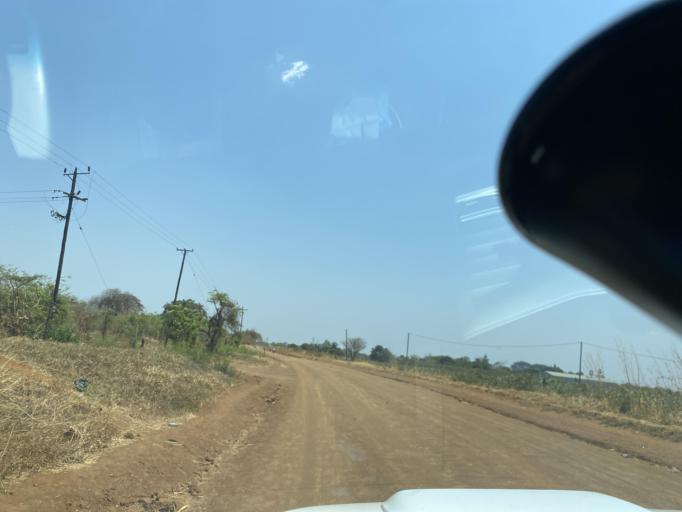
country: ZM
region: Lusaka
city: Lusaka
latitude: -15.4199
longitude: 28.1015
